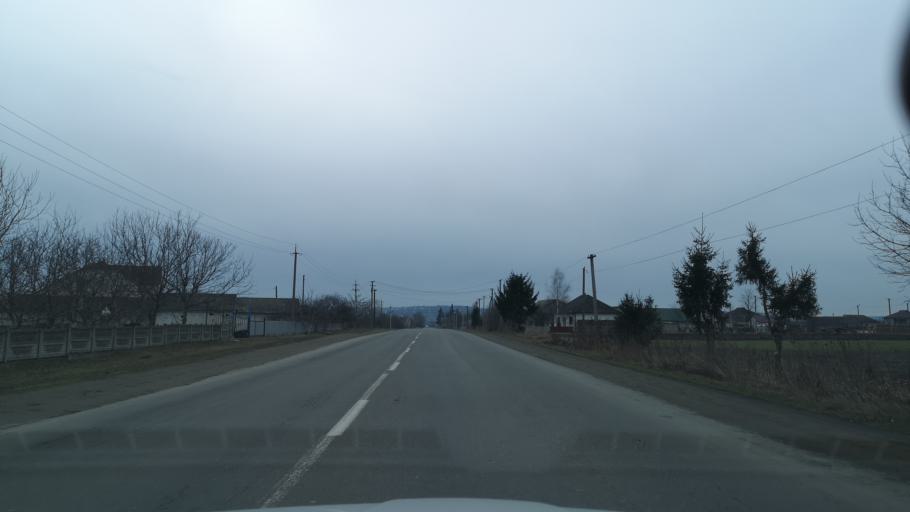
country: RO
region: Botosani
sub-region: Comuna Darabani
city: Bajura
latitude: 48.2413
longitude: 26.5482
